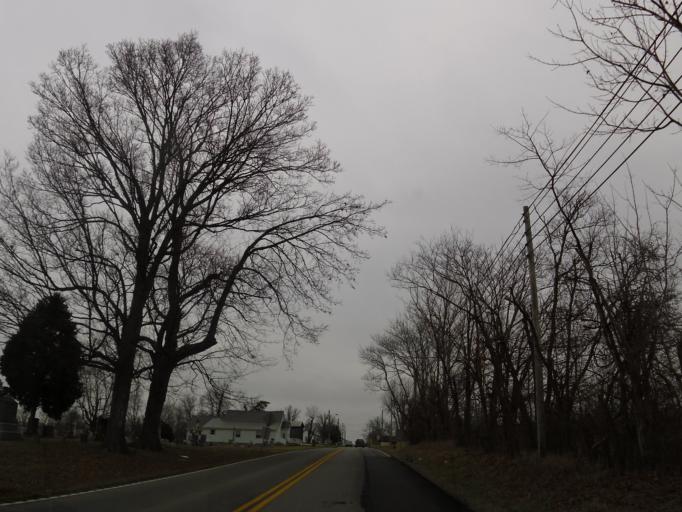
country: US
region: Kentucky
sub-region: Trimble County
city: Providence
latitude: 38.5225
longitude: -85.2199
